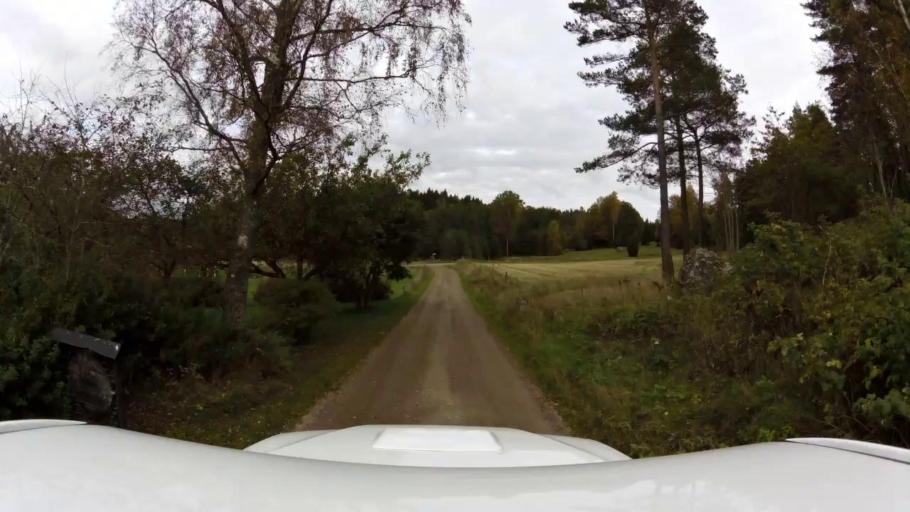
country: SE
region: OEstergoetland
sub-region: Linkopings Kommun
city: Ekangen
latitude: 58.5621
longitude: 15.6675
